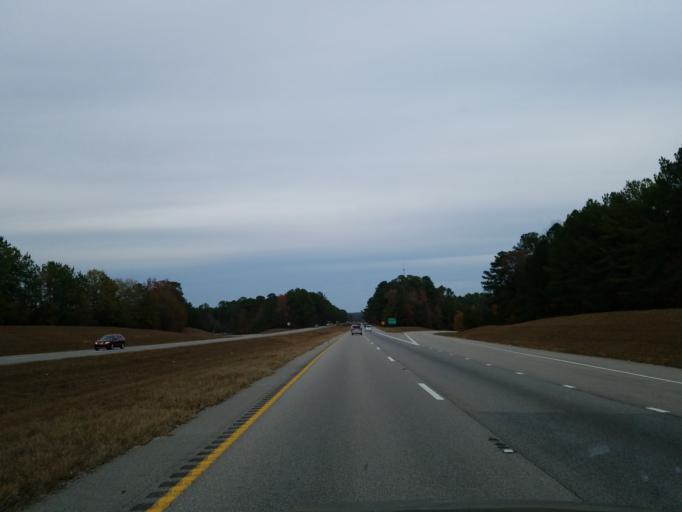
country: US
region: Mississippi
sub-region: Clarke County
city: Stonewall
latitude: 32.2010
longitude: -88.8464
